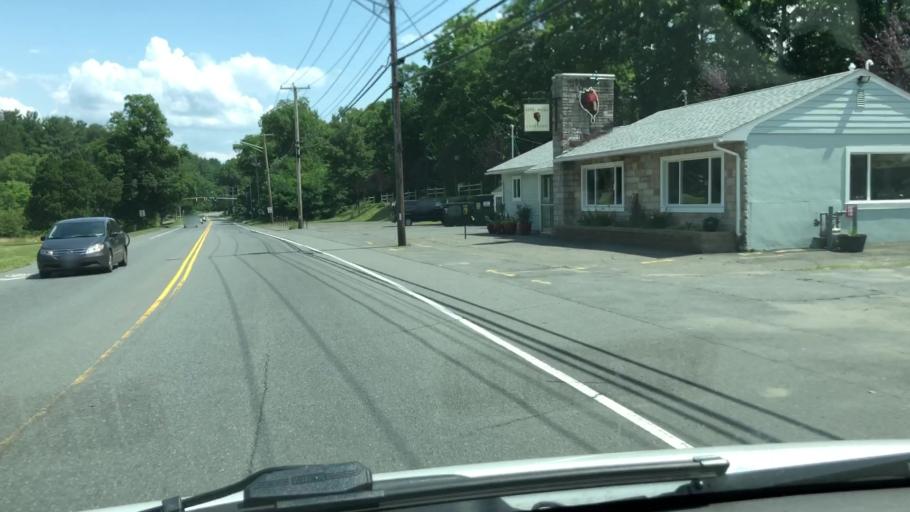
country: US
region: Massachusetts
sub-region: Hampshire County
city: Northampton
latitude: 42.3489
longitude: -72.6892
